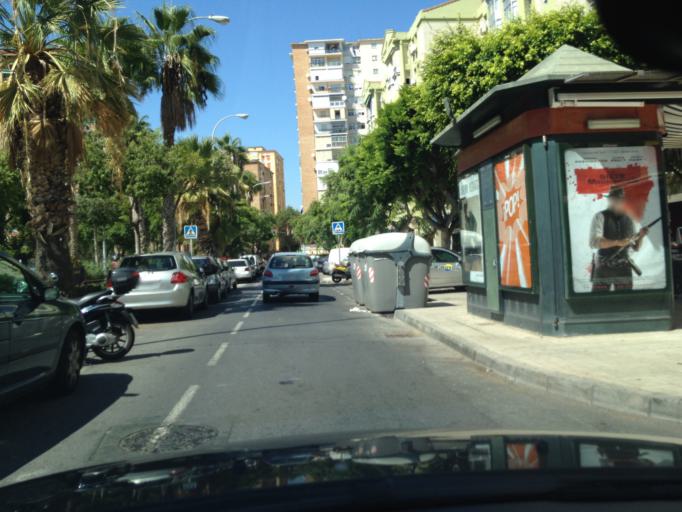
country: ES
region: Andalusia
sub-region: Provincia de Malaga
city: Malaga
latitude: 36.7044
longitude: -4.4355
